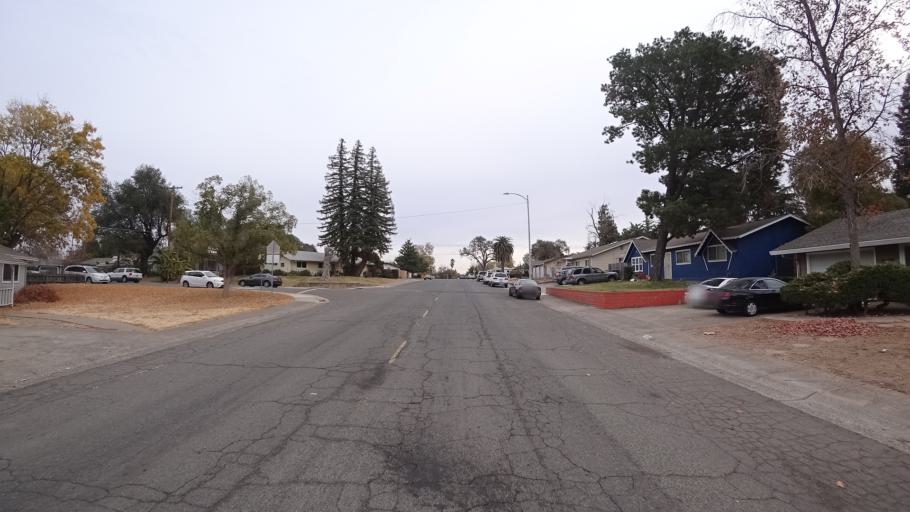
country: US
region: California
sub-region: Sacramento County
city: Citrus Heights
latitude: 38.7106
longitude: -121.2987
